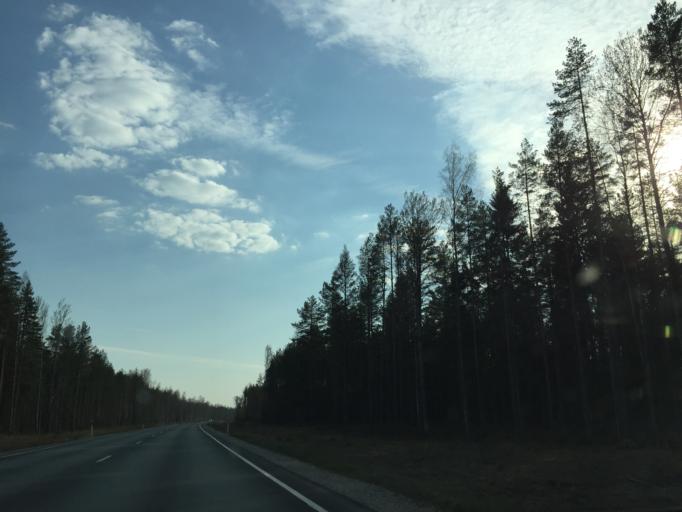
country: EE
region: Jogevamaa
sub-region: Mustvee linn
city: Mustvee
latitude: 58.8700
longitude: 26.9410
